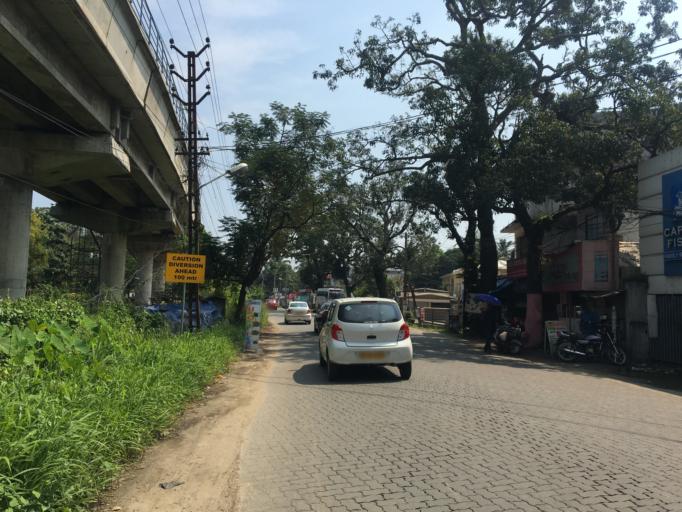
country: IN
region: Kerala
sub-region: Ernakulam
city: Cochin
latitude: 9.9617
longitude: 76.3208
